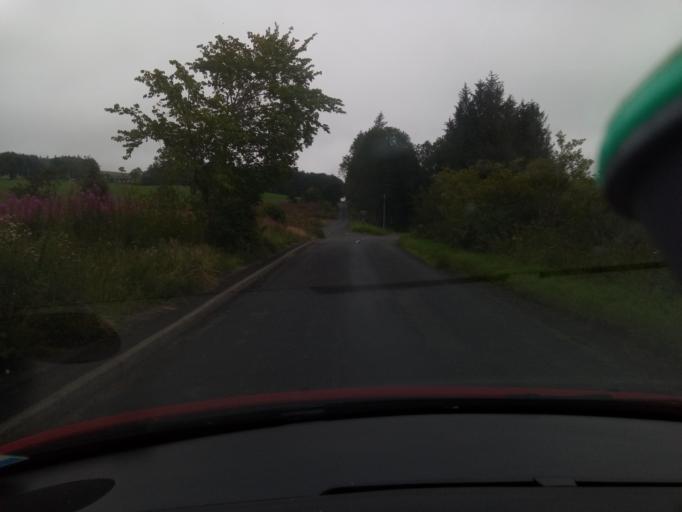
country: GB
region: Scotland
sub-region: Fife
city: Pathhead
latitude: 55.7352
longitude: -2.9113
